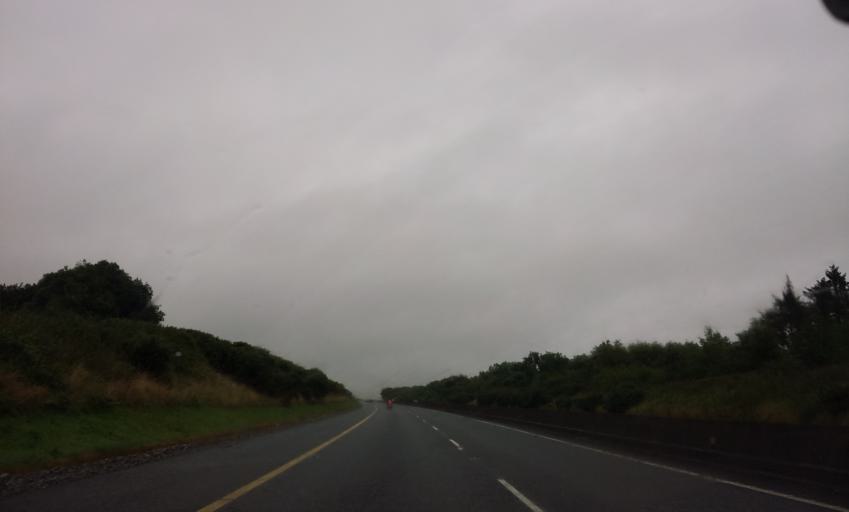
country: IE
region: Munster
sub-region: County Cork
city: Fermoy
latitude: 52.1920
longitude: -8.2720
